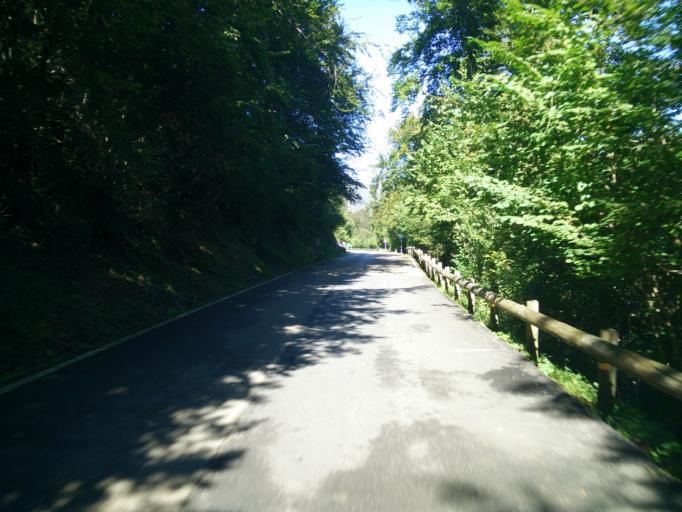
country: ES
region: Cantabria
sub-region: Provincia de Cantabria
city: Ruente
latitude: 43.1117
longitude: -4.2845
